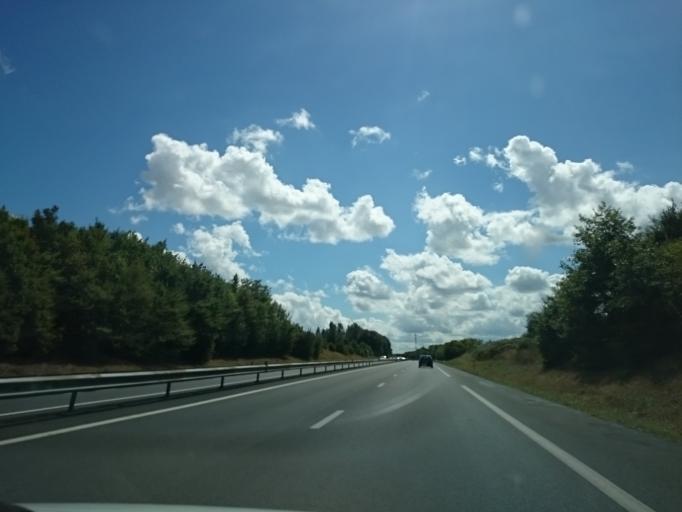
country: FR
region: Pays de la Loire
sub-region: Departement de Maine-et-Loire
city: Durtal
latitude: 47.7289
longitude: -0.2497
